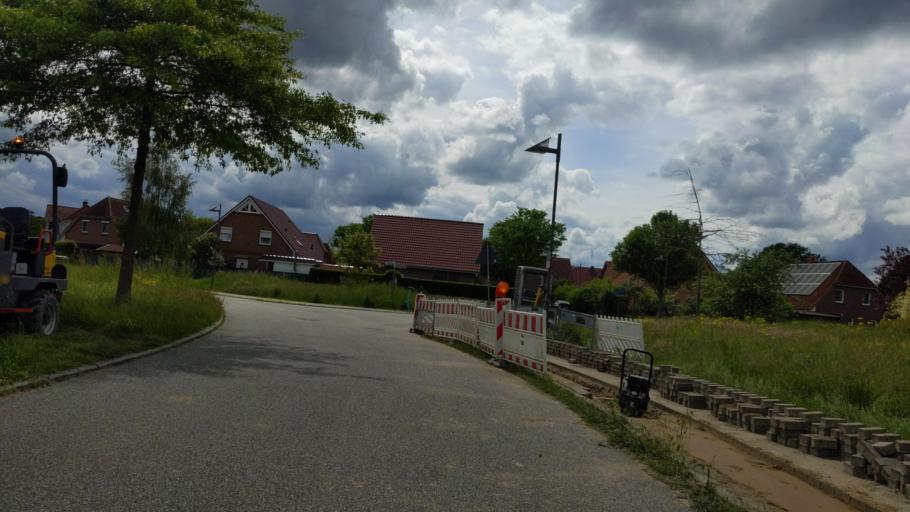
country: DE
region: Schleswig-Holstein
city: Luebeck
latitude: 53.8244
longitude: 10.6834
